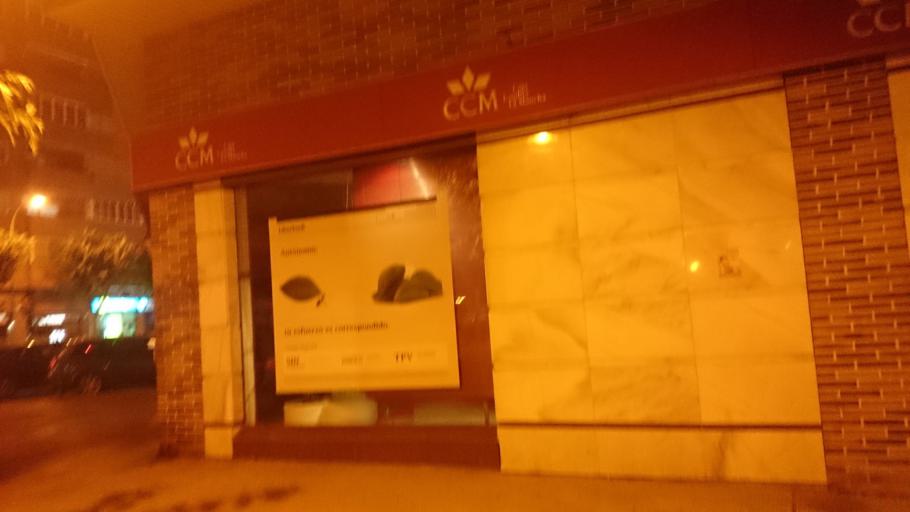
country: ES
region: Madrid
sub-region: Provincia de Madrid
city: Coslada
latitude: 40.4288
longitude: -3.5606
